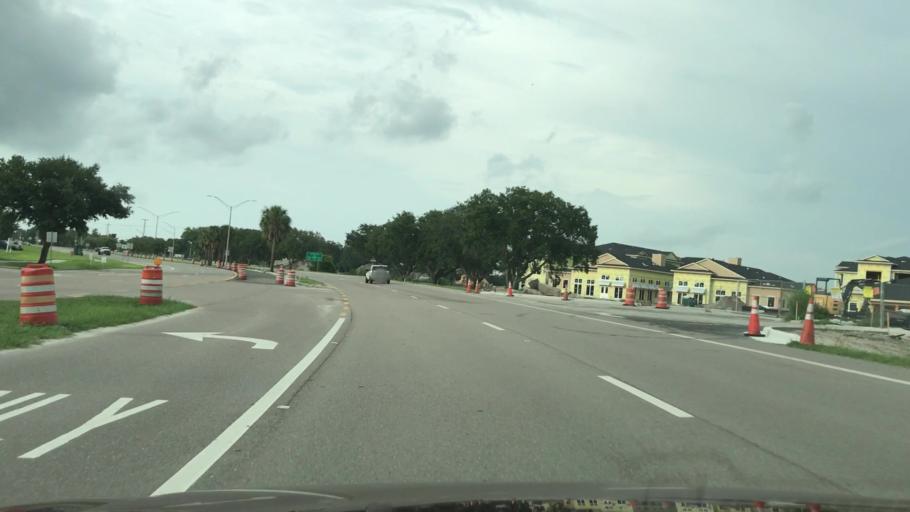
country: US
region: Florida
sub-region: Sarasota County
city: Plantation
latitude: 27.0958
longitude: -82.3849
